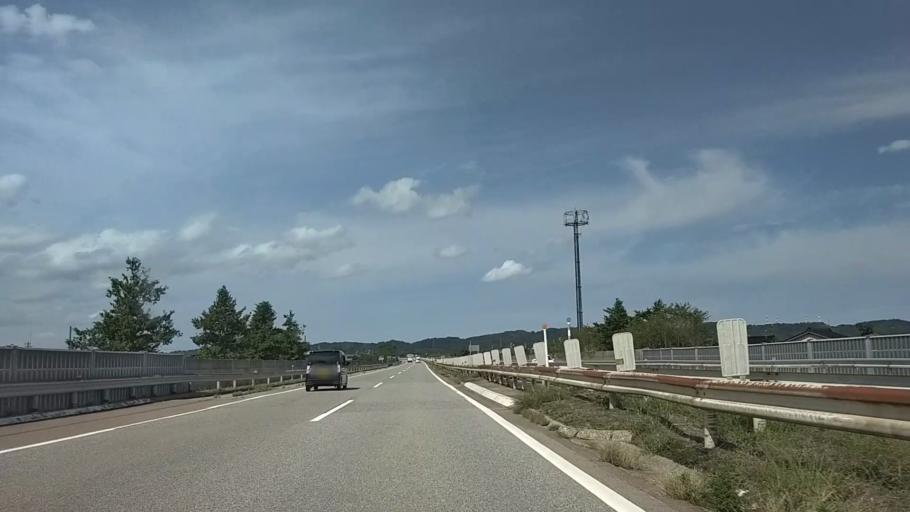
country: JP
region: Toyama
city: Toyama-shi
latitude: 36.6675
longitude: 137.1832
